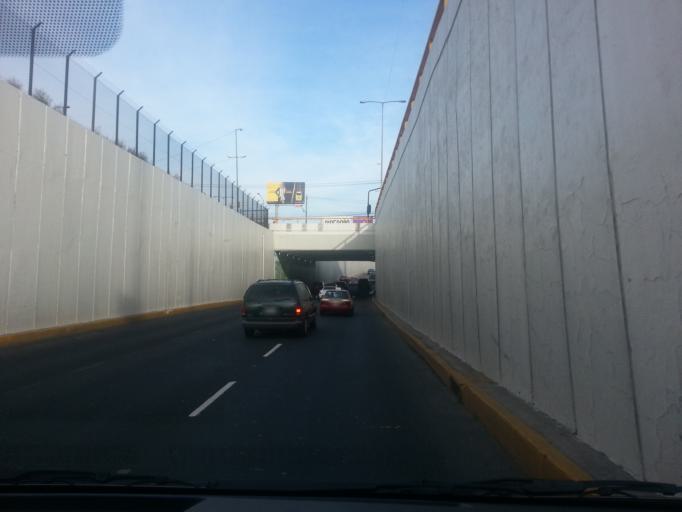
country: MX
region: Mexico City
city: Cuauhtemoc
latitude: 19.4614
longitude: -99.1267
